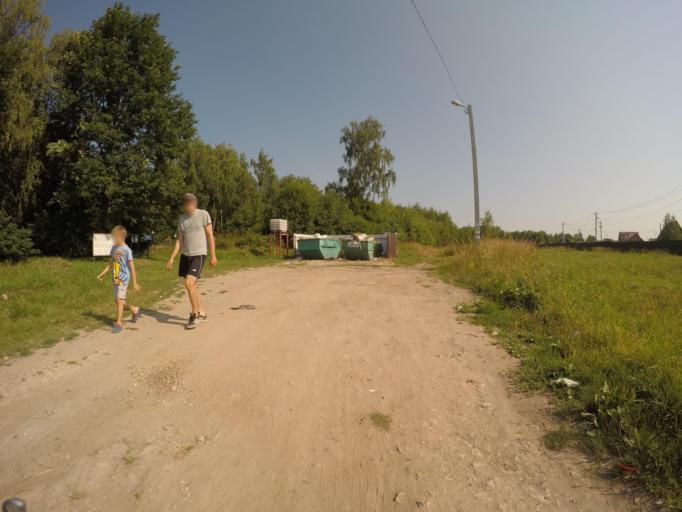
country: RU
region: Moskovskaya
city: Rechitsy
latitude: 55.6134
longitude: 38.5189
